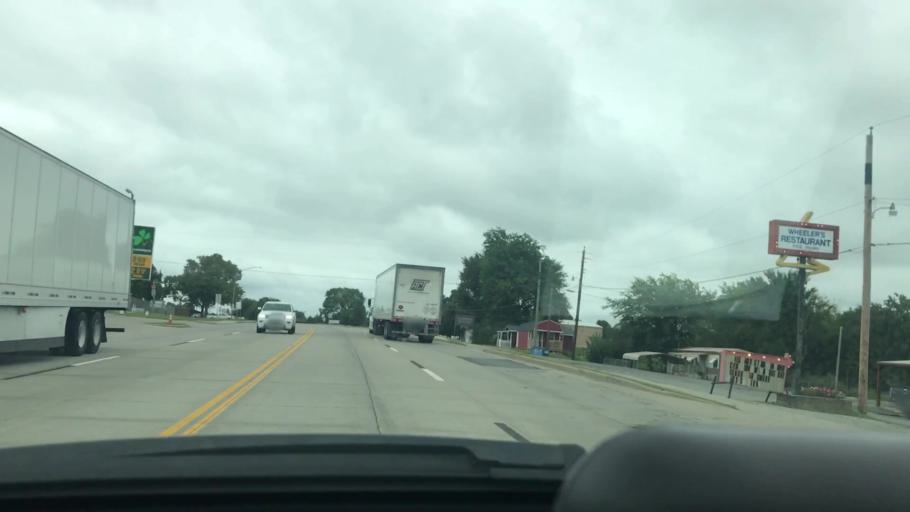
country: US
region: Oklahoma
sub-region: Pittsburg County
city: McAlester
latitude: 34.7229
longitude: -95.8987
